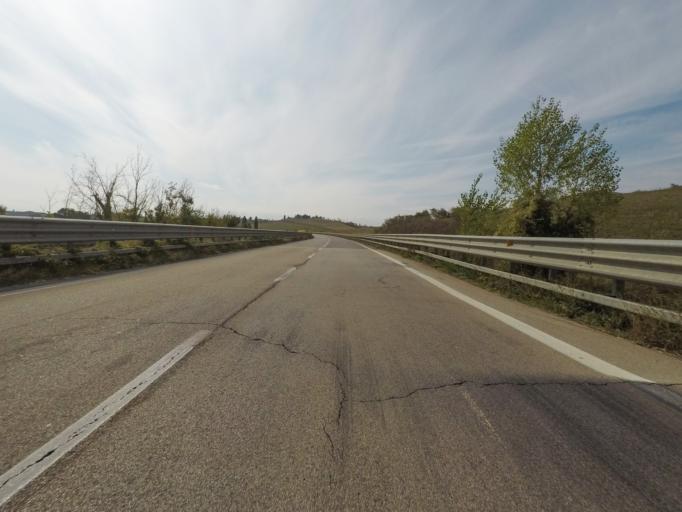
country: IT
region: Tuscany
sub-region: Provincia di Siena
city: Siena
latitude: 43.2874
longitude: 11.3335
